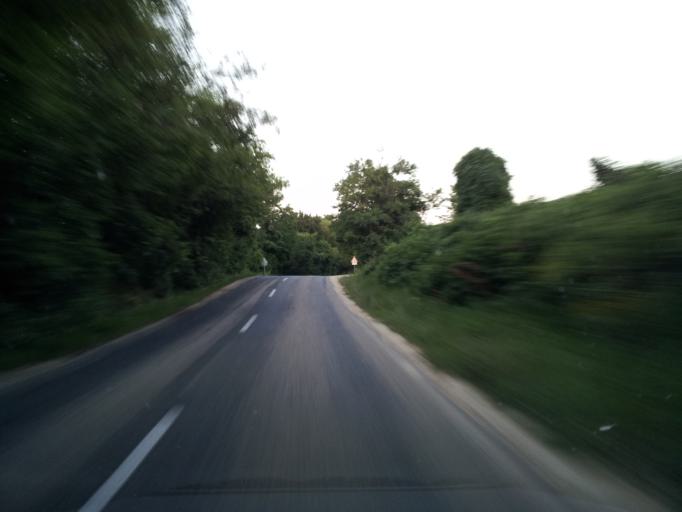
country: HU
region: Fejer
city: Szarliget
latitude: 47.5148
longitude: 18.5354
